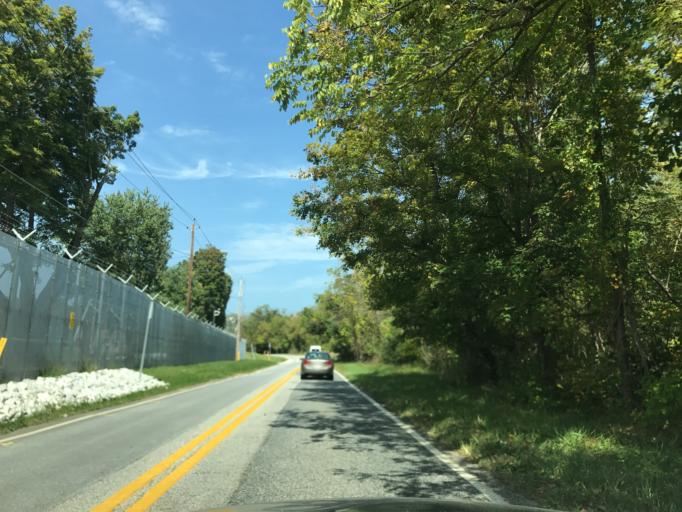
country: US
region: Maryland
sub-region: Baltimore County
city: Cockeysville
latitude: 39.4931
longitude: -76.6802
